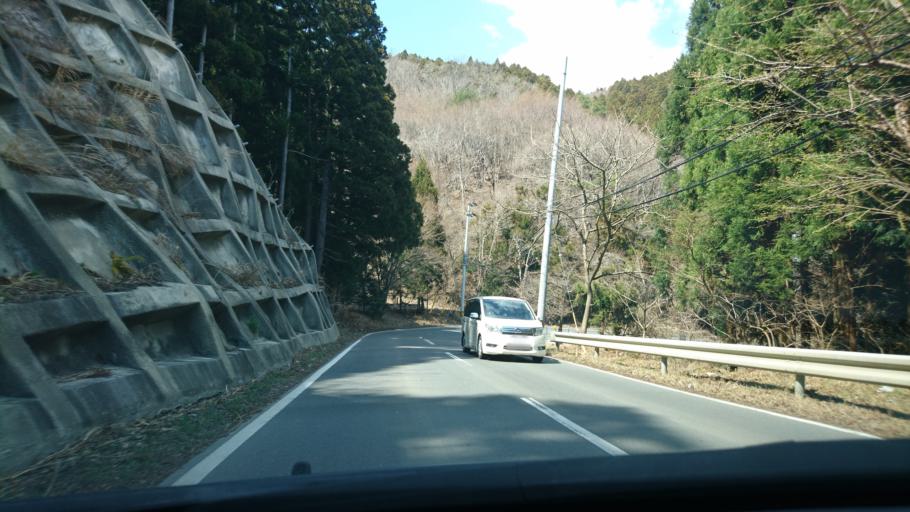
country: JP
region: Miyagi
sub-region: Oshika Gun
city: Onagawa Cho
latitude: 38.4403
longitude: 141.4699
